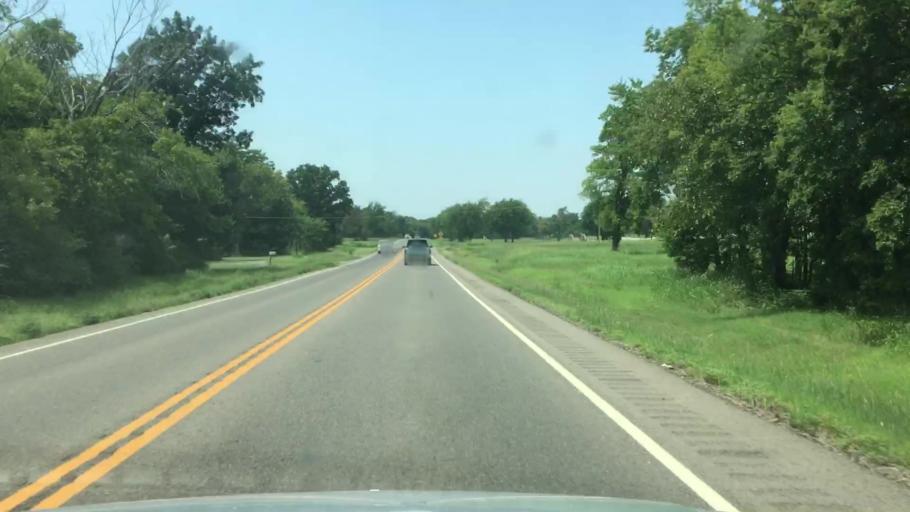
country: US
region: Oklahoma
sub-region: Wagoner County
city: Wagoner
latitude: 35.9383
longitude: -95.3100
